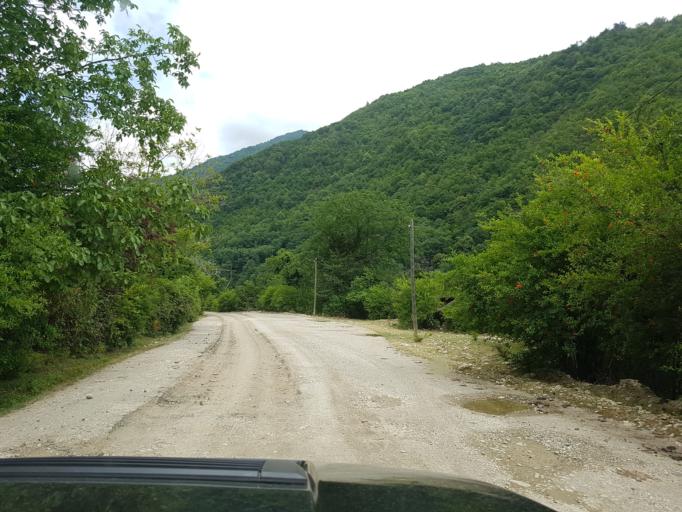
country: GE
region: Imereti
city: Tsqaltubo
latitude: 42.4784
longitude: 42.7670
